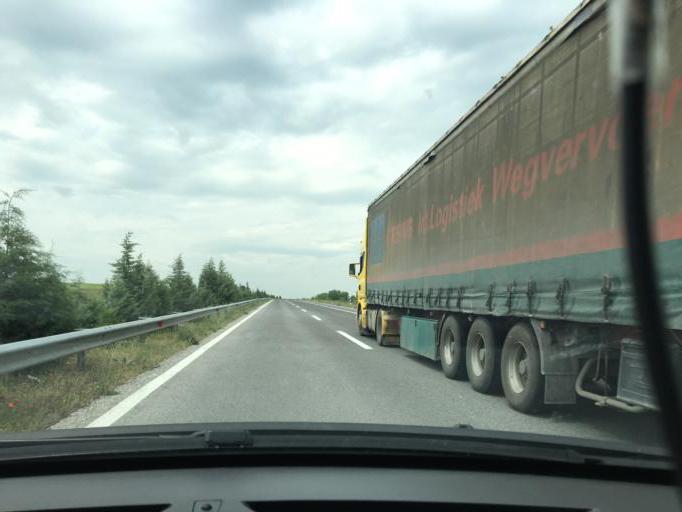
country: MK
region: Negotino
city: Negotino
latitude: 41.4649
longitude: 22.1263
